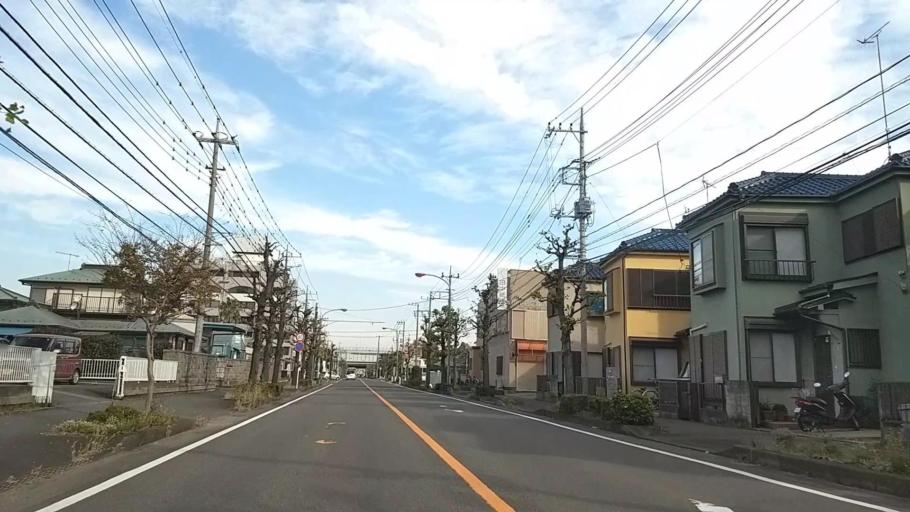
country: JP
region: Kanagawa
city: Atsugi
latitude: 35.4193
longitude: 139.3648
